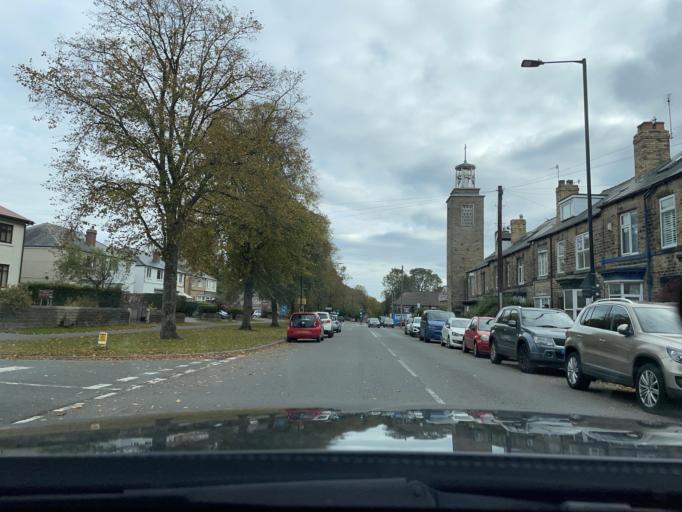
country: GB
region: England
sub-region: Sheffield
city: Sheffield
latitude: 53.3804
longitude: -1.5212
